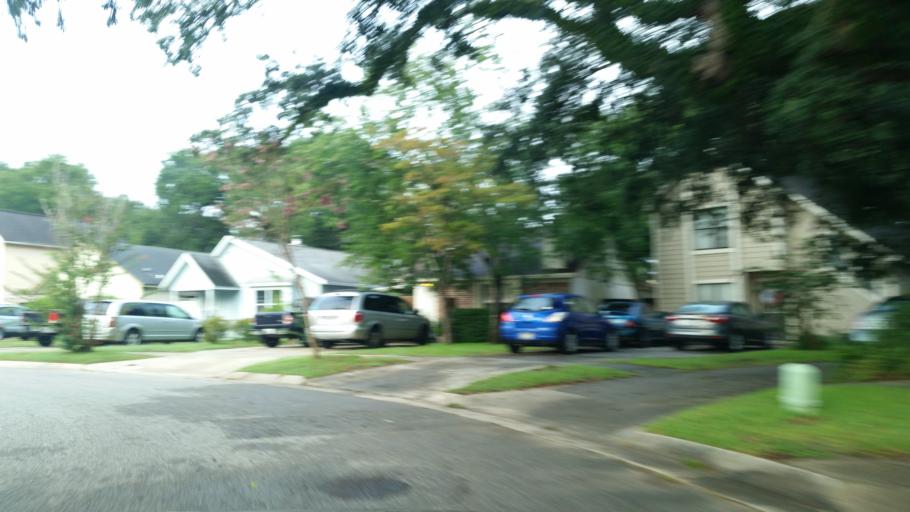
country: US
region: Florida
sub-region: Escambia County
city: Ferry Pass
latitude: 30.5073
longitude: -87.1988
